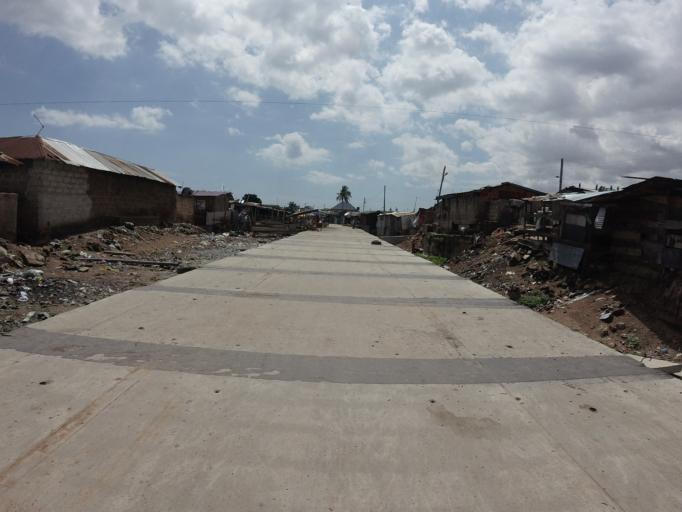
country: GH
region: Greater Accra
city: Accra
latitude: 5.5905
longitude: -0.1921
